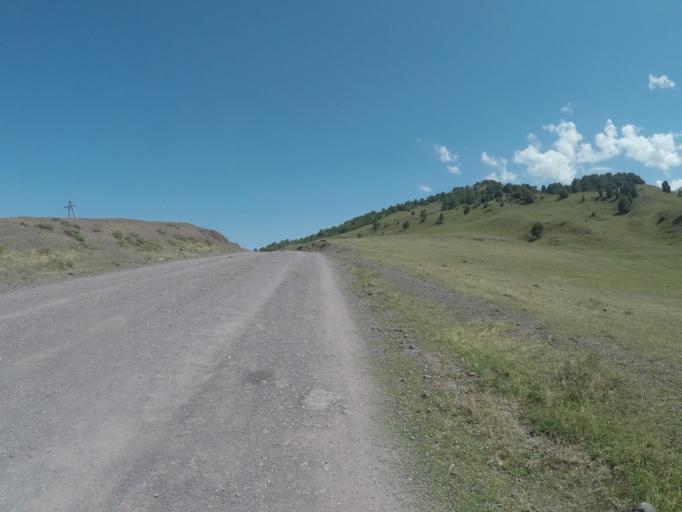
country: KG
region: Chuy
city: Bishkek
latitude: 42.6498
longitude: 74.5324
